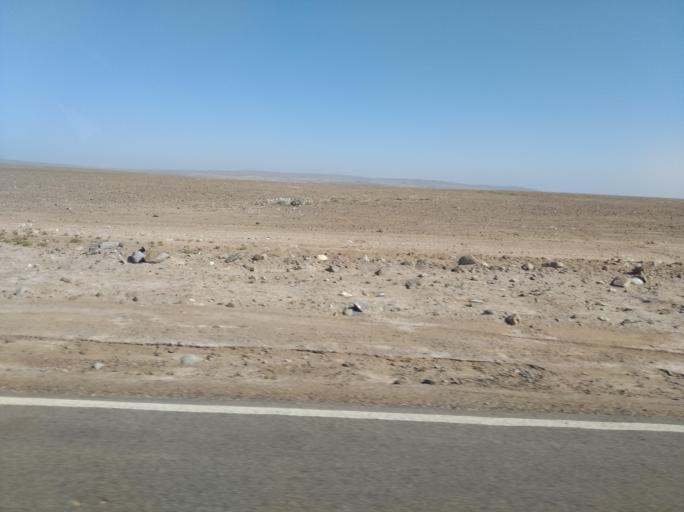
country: CL
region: Atacama
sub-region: Provincia de Copiapo
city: Copiapo
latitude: -27.3165
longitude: -70.8613
